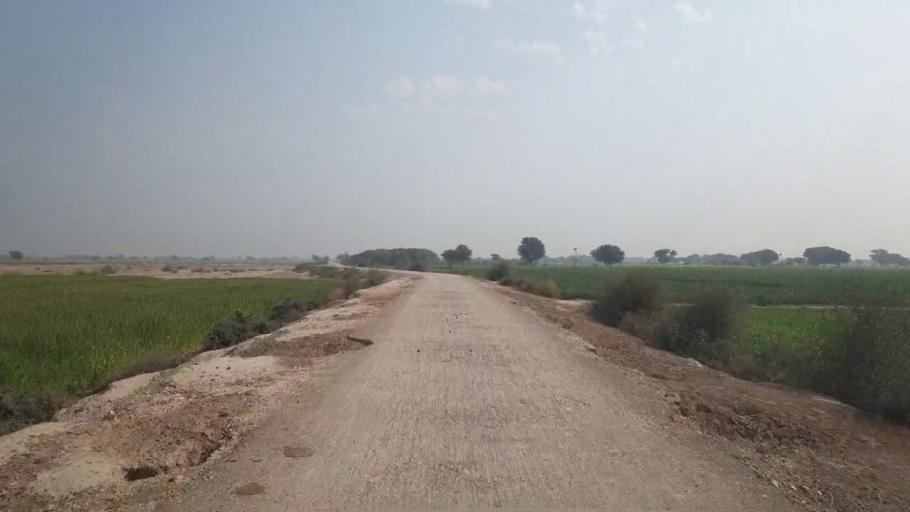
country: PK
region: Sindh
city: Hala
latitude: 25.7640
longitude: 68.4220
